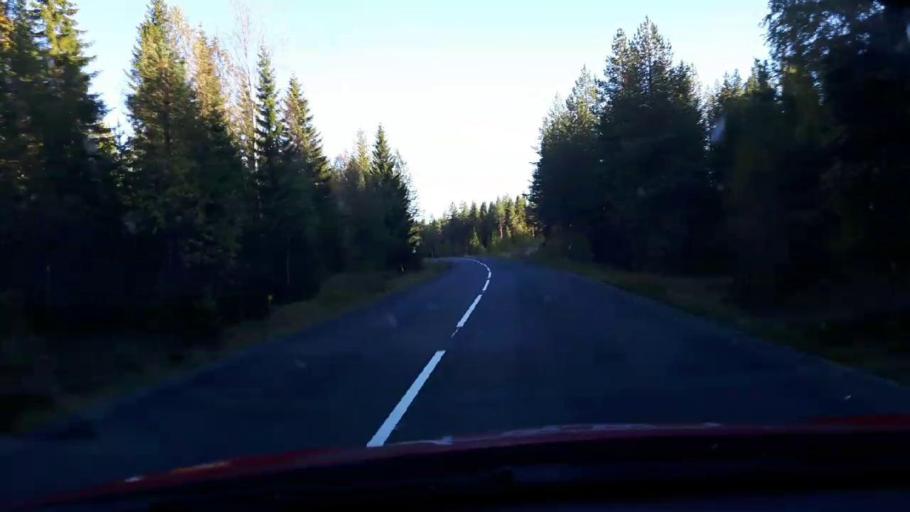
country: SE
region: Jaemtland
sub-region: OEstersunds Kommun
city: Lit
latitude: 63.4172
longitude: 14.8725
